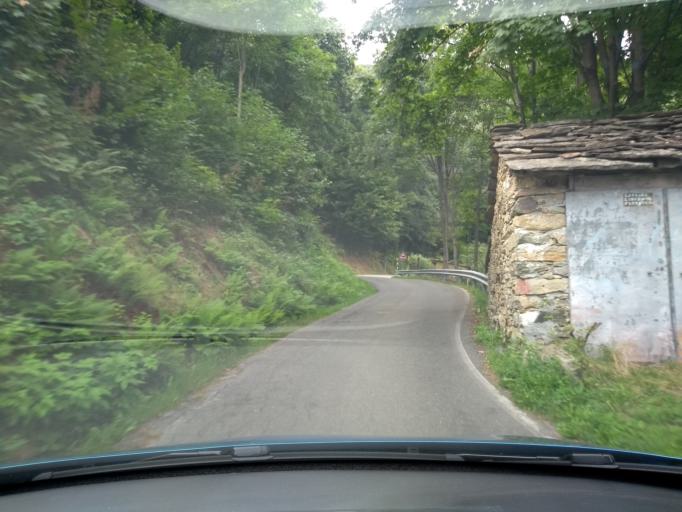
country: IT
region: Piedmont
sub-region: Provincia di Torino
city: Corio
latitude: 45.3266
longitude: 7.5179
